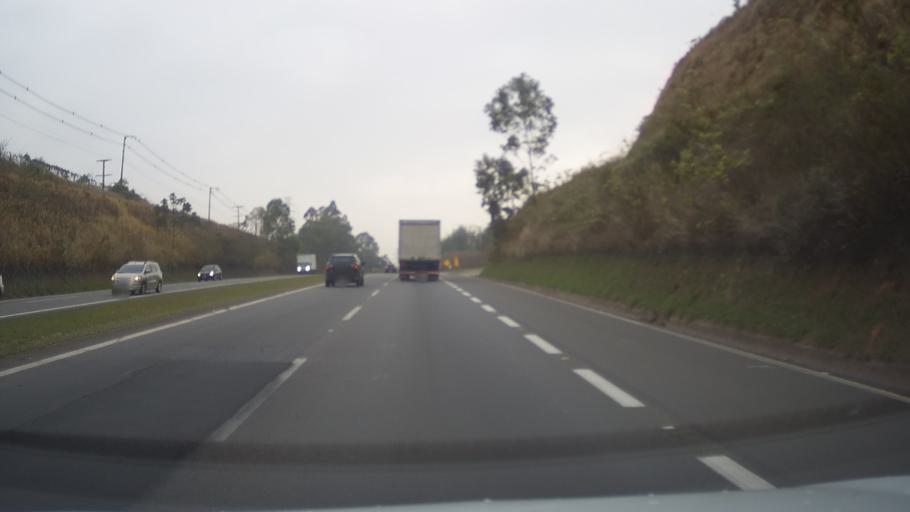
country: BR
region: Sao Paulo
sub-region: Jundiai
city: Jundiai
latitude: -23.1578
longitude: -46.8951
